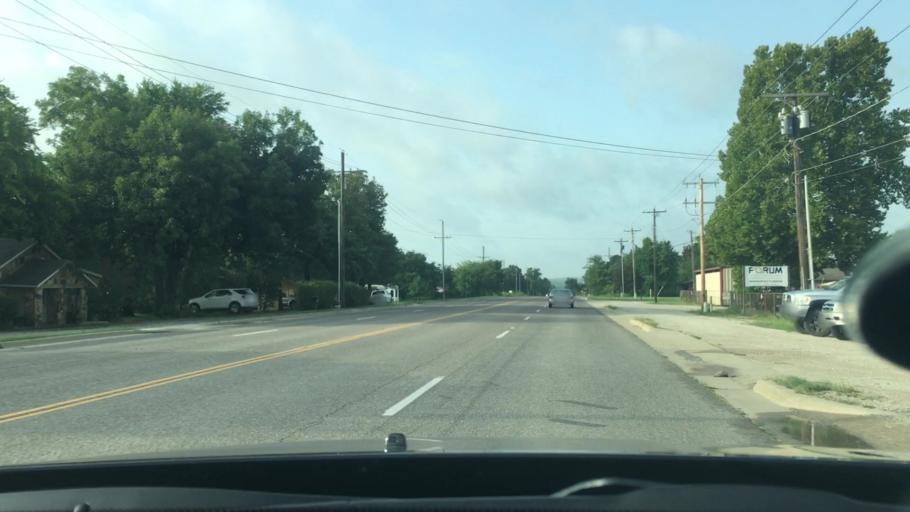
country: US
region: Oklahoma
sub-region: Murray County
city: Davis
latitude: 34.4812
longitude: -97.1310
